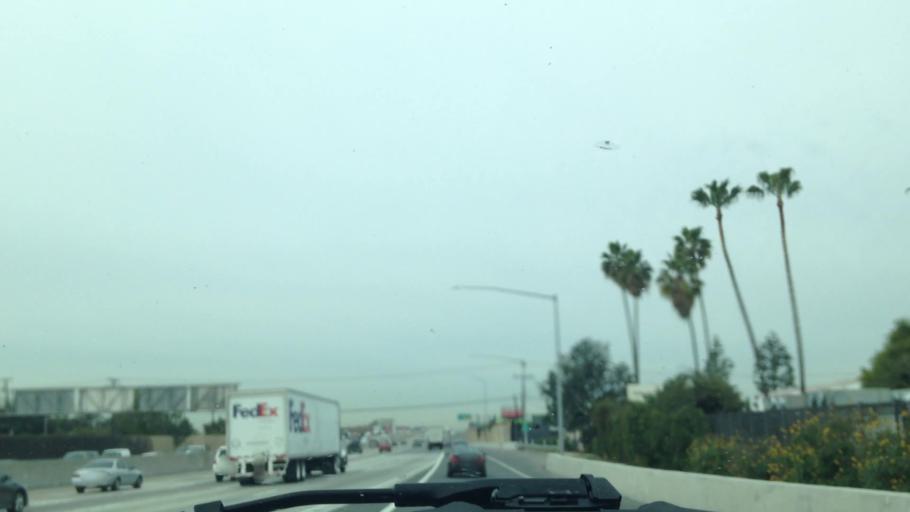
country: US
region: California
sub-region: Orange County
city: Placentia
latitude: 33.8545
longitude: -117.8920
